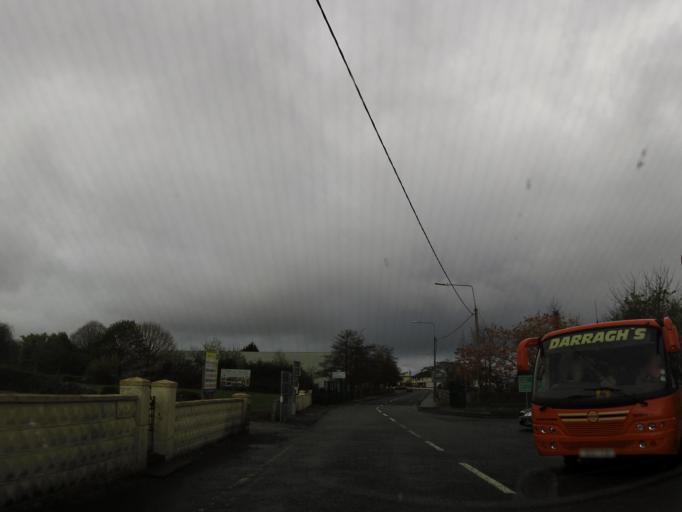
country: IE
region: Connaught
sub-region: Sligo
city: Tobercurry
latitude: 54.0511
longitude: -8.7354
